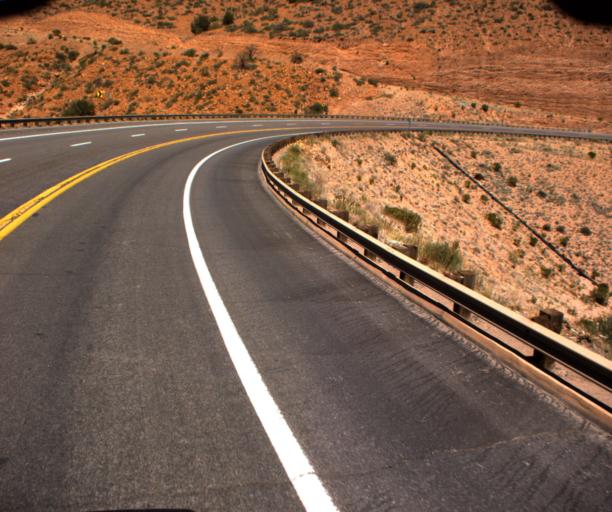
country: US
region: Arizona
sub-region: Greenlee County
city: Clifton
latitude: 33.0661
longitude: -109.3296
